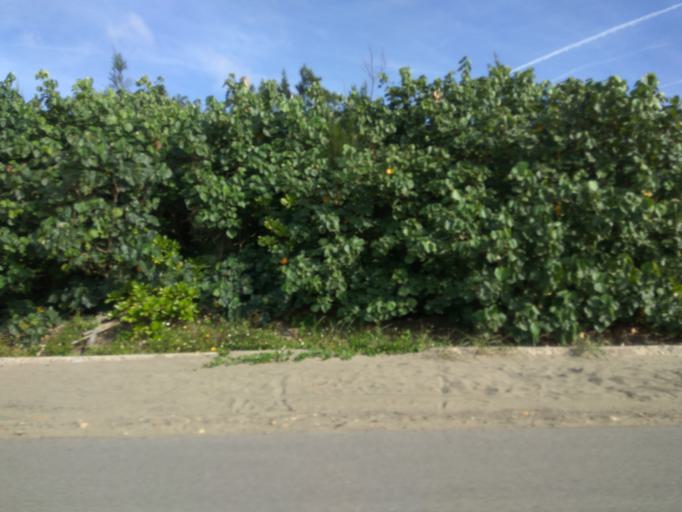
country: TW
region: Taiwan
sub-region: Hsinchu
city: Zhubei
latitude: 24.9827
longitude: 121.0159
